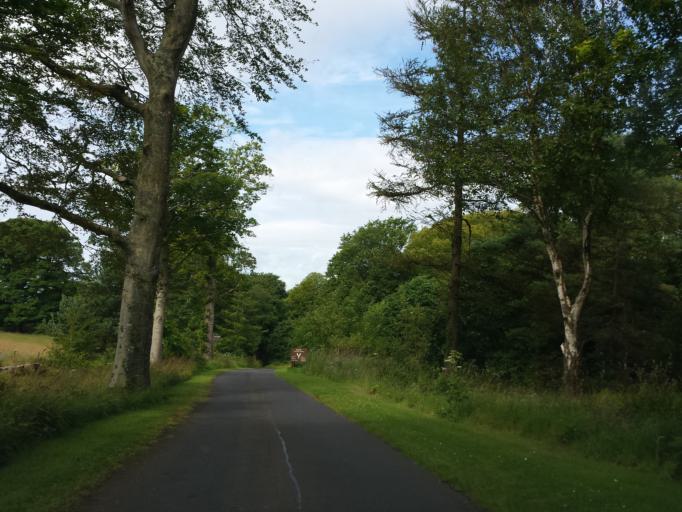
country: GB
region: Scotland
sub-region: South Ayrshire
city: Maybole
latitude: 55.3541
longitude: -4.7803
